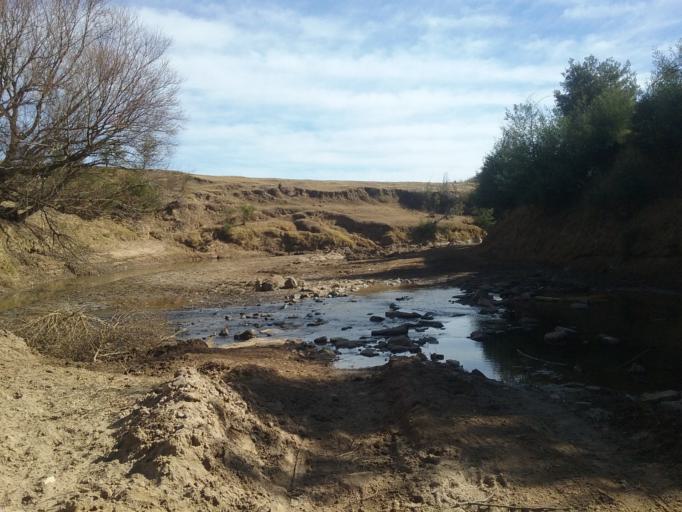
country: LS
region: Maseru
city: Maseru
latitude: -29.4367
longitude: 27.5935
